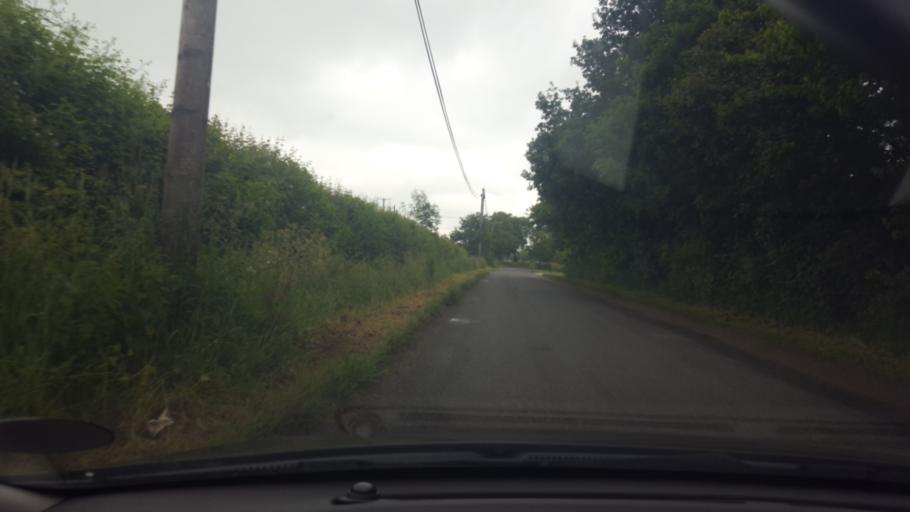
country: GB
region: England
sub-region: Essex
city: Great Bentley
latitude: 51.8793
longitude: 1.0829
